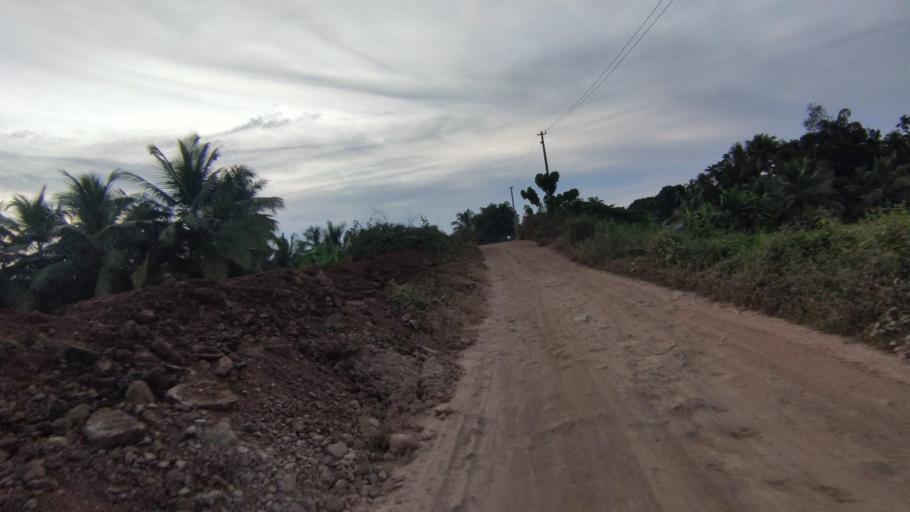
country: IN
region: Kerala
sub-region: Kottayam
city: Kottayam
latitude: 9.6471
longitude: 76.4798
